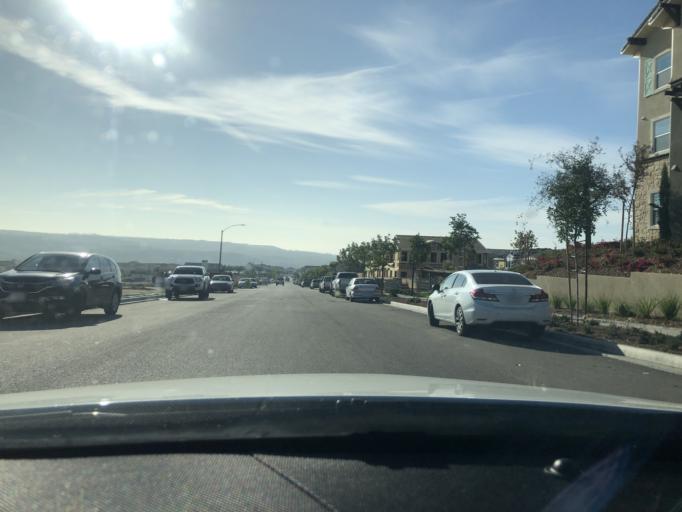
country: US
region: California
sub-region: San Diego County
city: Bonita
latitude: 32.5989
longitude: -116.9997
